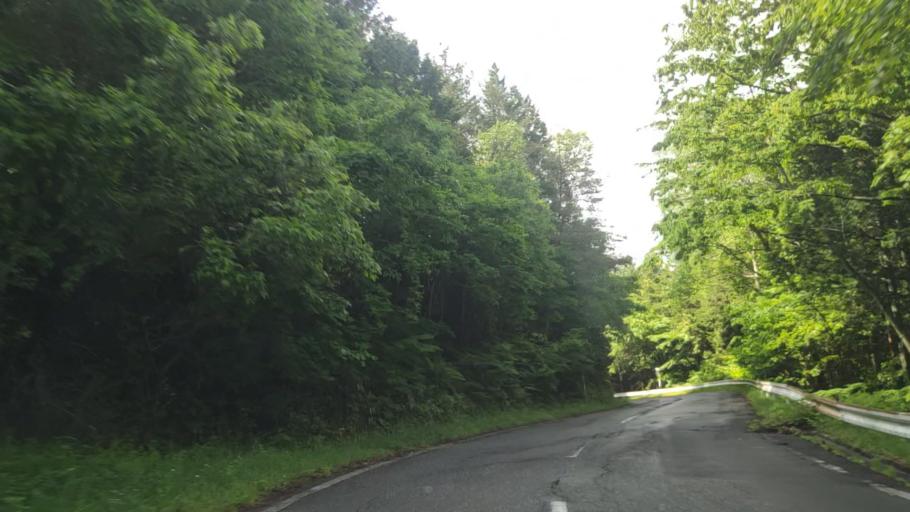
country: JP
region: Nagano
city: Suwa
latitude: 36.0908
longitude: 138.1463
